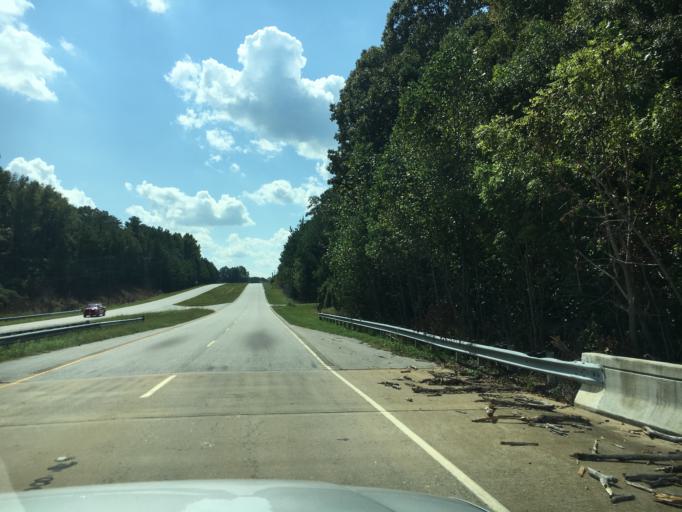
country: US
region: South Carolina
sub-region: Spartanburg County
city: Roebuck
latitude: 34.8131
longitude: -82.0016
